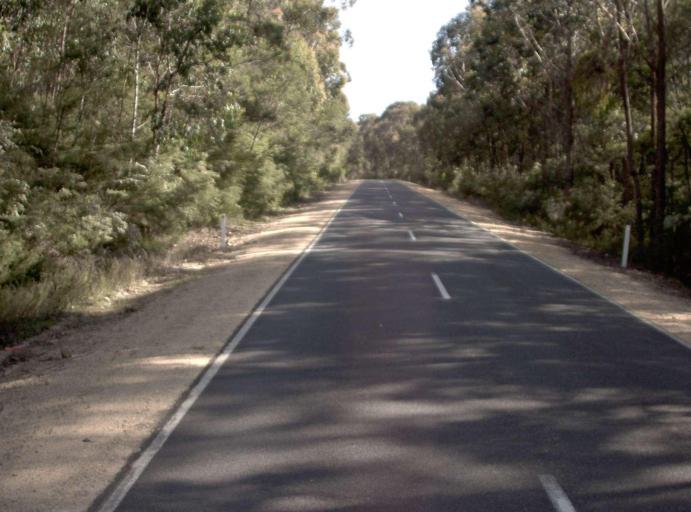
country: AU
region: Victoria
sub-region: East Gippsland
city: Lakes Entrance
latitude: -37.6431
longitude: 148.1092
